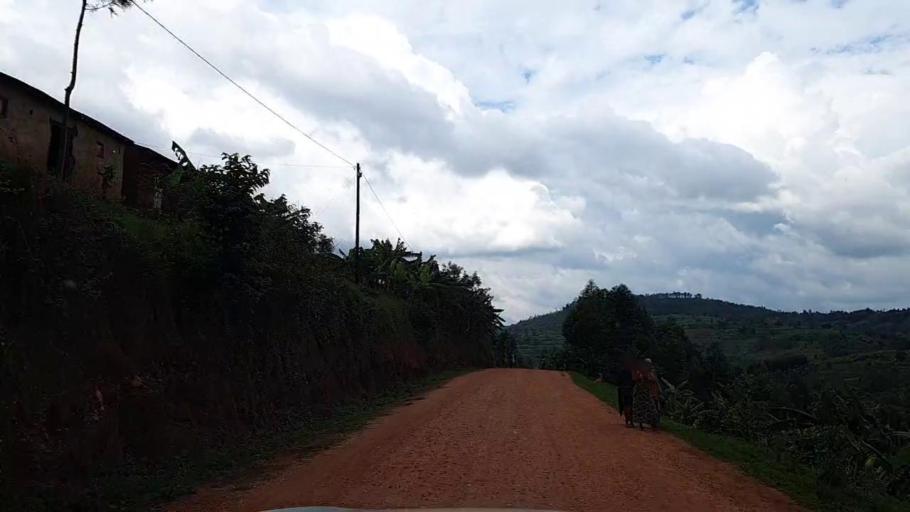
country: RW
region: Southern Province
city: Nyanza
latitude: -2.4146
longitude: 29.6703
